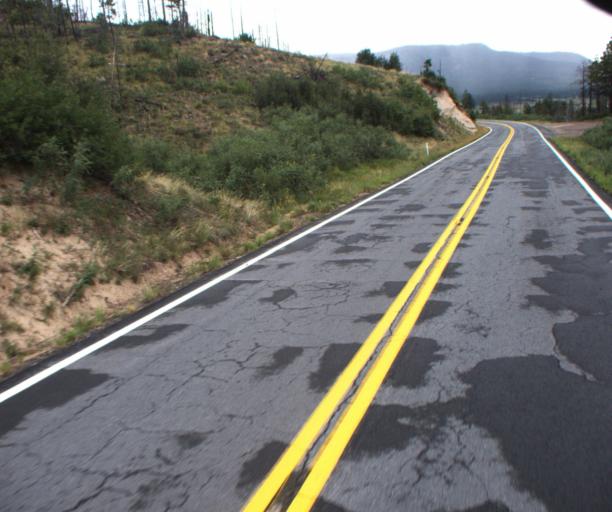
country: US
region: Arizona
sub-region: Apache County
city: Eagar
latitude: 33.8174
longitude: -109.1571
